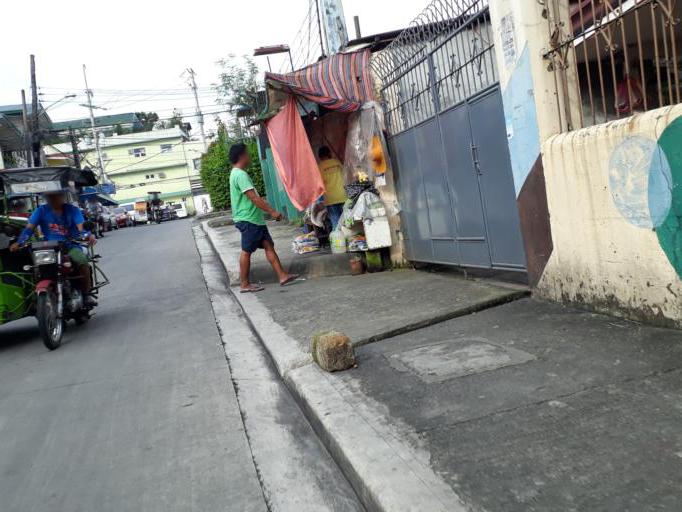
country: PH
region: Metro Manila
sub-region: Caloocan City
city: Niugan
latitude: 14.6744
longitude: 120.9838
